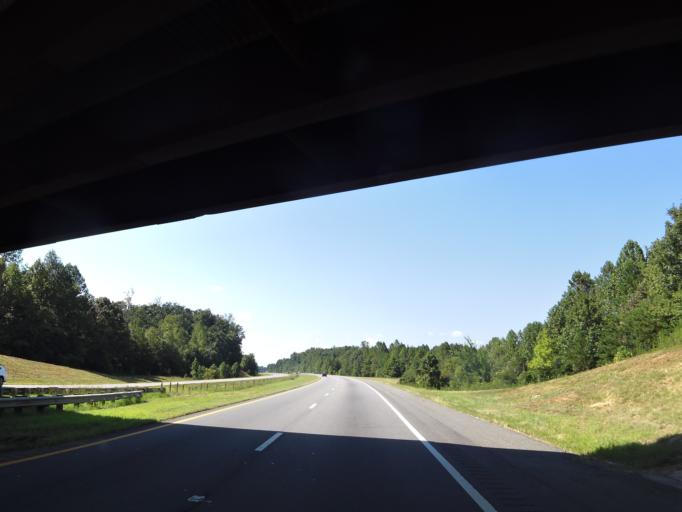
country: US
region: North Carolina
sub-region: Catawba County
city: Mountain View
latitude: 35.6567
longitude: -81.3175
